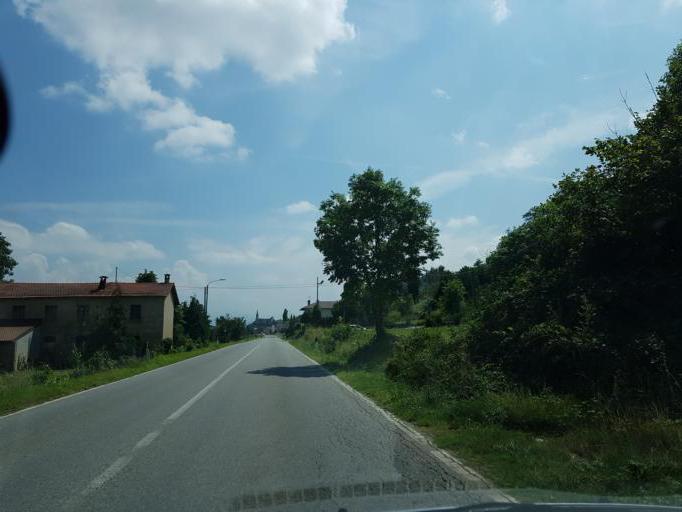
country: IT
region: Piedmont
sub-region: Provincia di Cuneo
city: Caraglio
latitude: 44.4297
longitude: 7.4246
